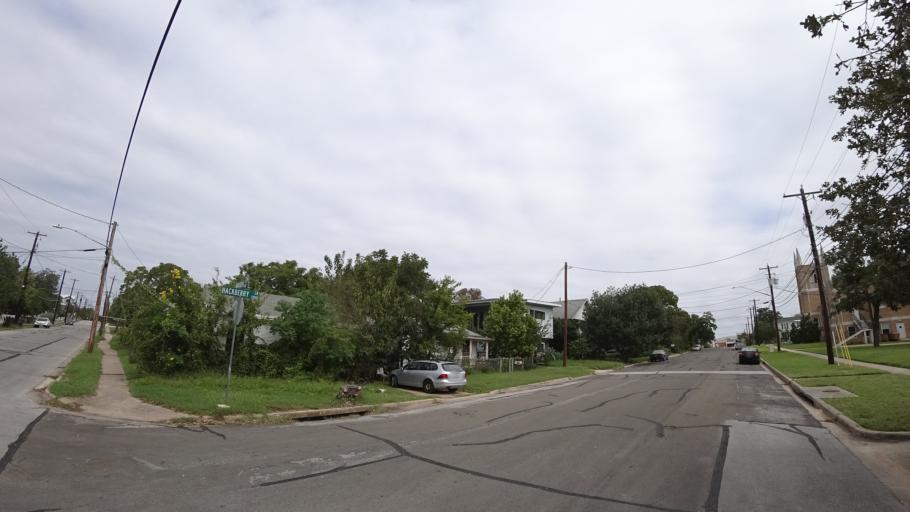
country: US
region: Texas
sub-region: Travis County
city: Austin
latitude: 30.2698
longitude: -97.7271
